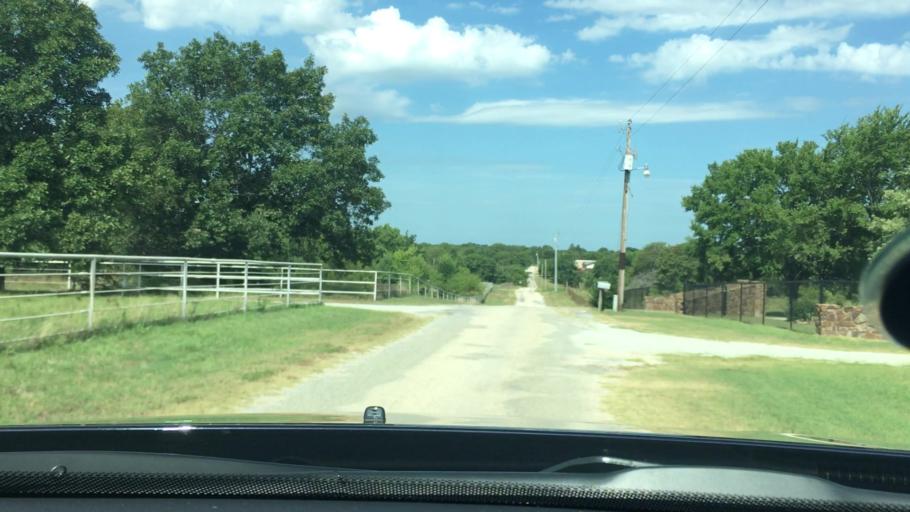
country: US
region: Oklahoma
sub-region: Pontotoc County
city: Ada
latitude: 34.7653
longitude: -96.5590
